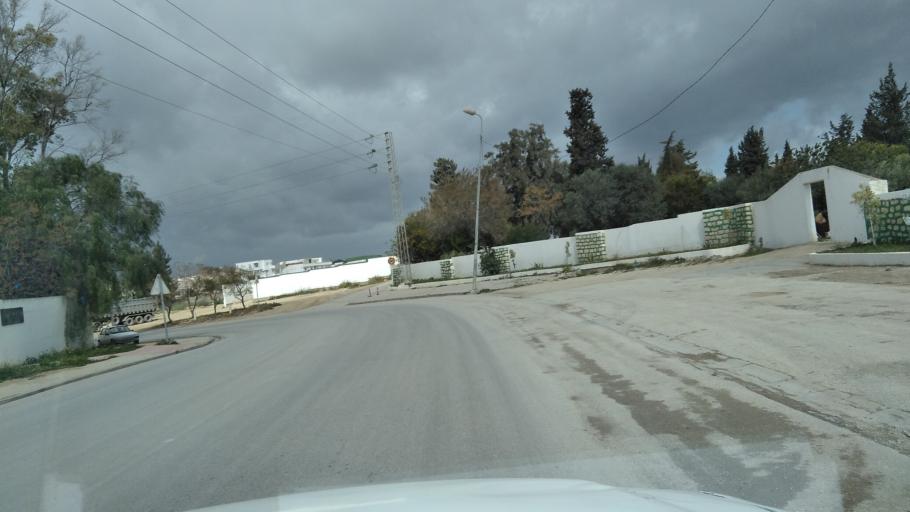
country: TN
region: Bin 'Arus
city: Ben Arous
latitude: 36.7440
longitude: 10.2285
